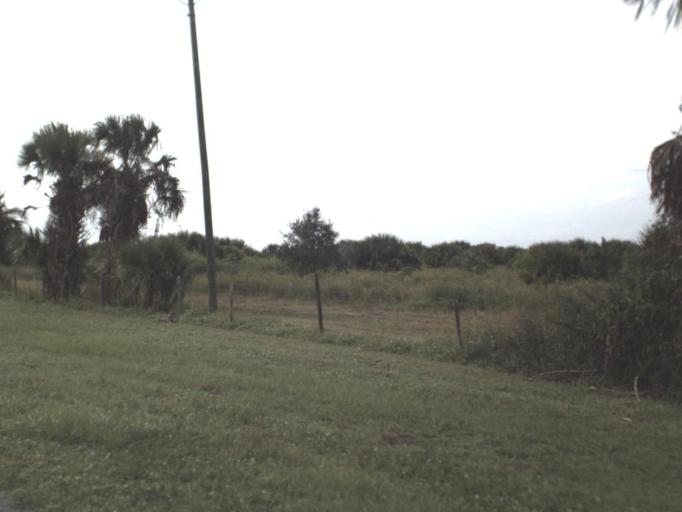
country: US
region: Florida
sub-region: Hendry County
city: Port LaBelle
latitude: 26.7685
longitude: -81.2835
